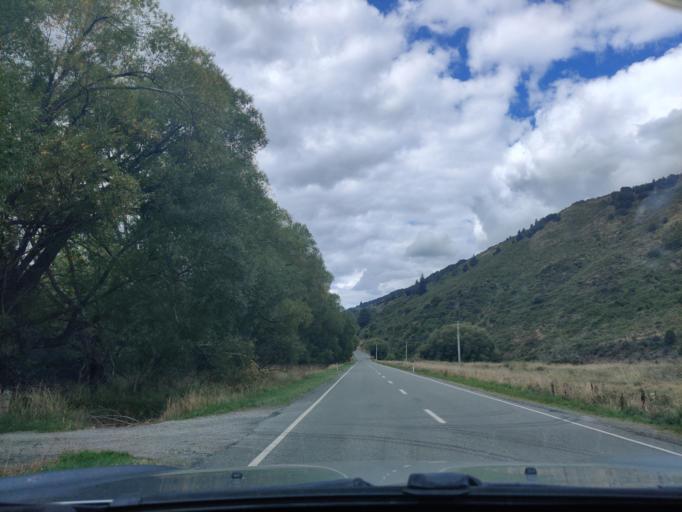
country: NZ
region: Canterbury
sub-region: Hurunui District
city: Amberley
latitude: -42.5956
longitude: 172.5513
